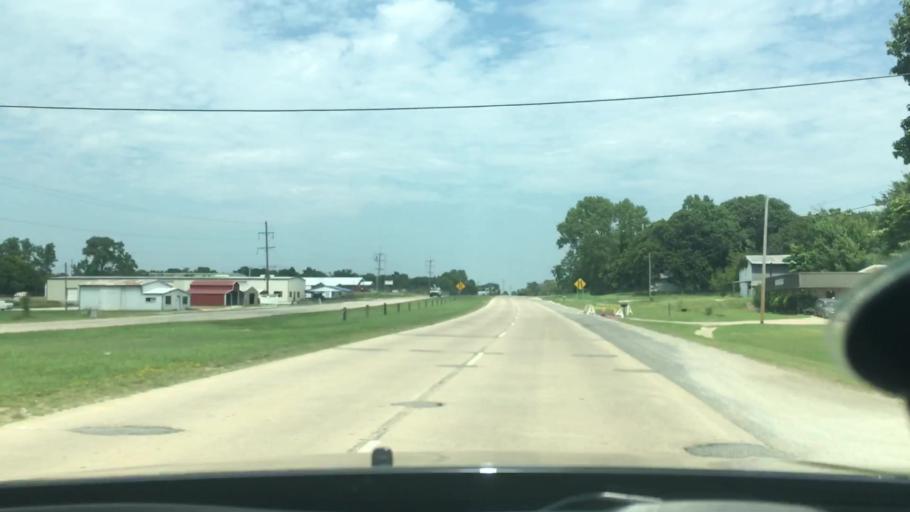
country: US
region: Oklahoma
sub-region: Pontotoc County
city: Ada
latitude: 34.8116
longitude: -96.6782
